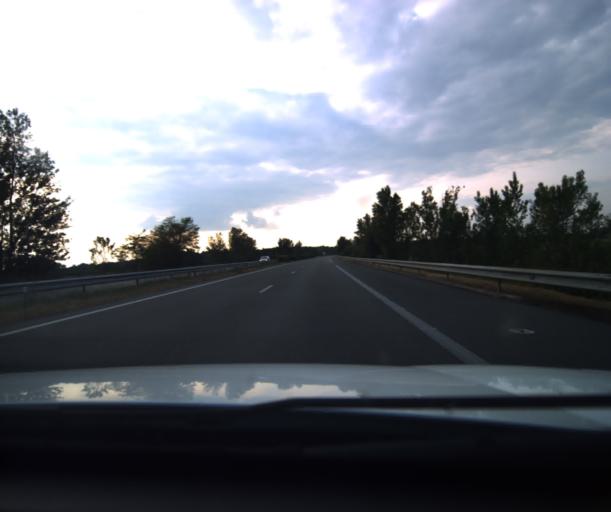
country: FR
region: Midi-Pyrenees
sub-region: Departement du Tarn-et-Garonne
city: Montech
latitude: 43.9851
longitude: 1.2447
